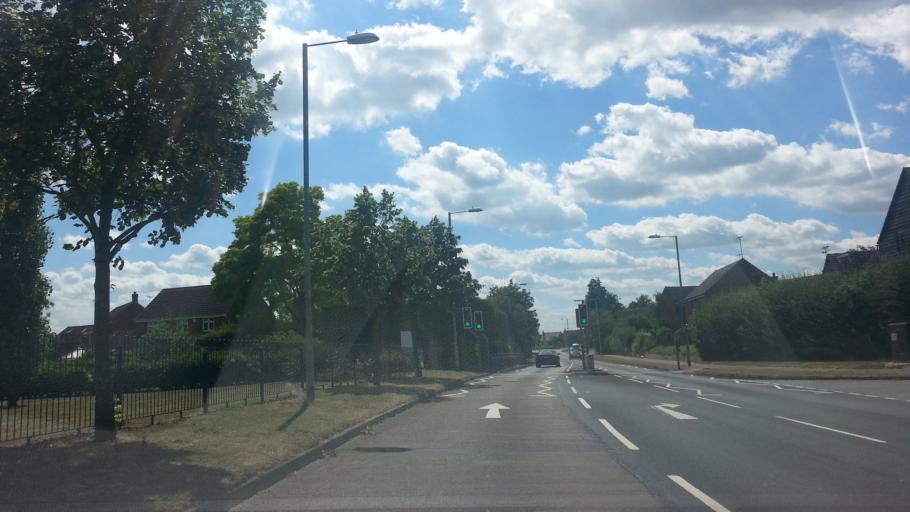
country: GB
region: England
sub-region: Essex
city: Chelmsford
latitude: 51.7356
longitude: 0.5109
